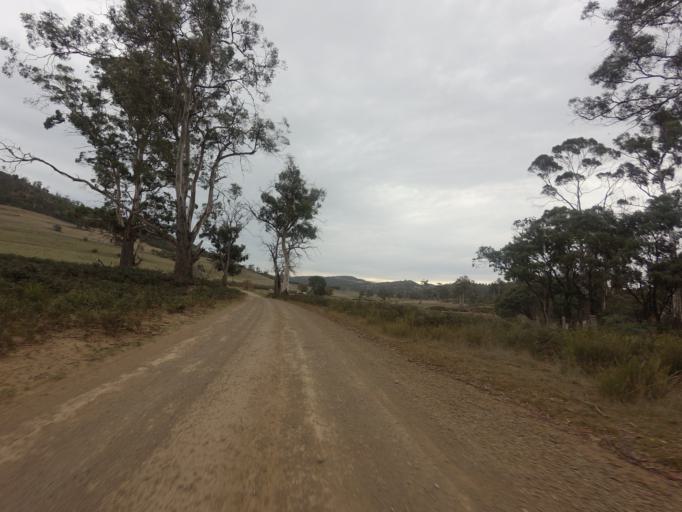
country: AU
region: Tasmania
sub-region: Derwent Valley
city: New Norfolk
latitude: -42.5535
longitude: 146.9607
